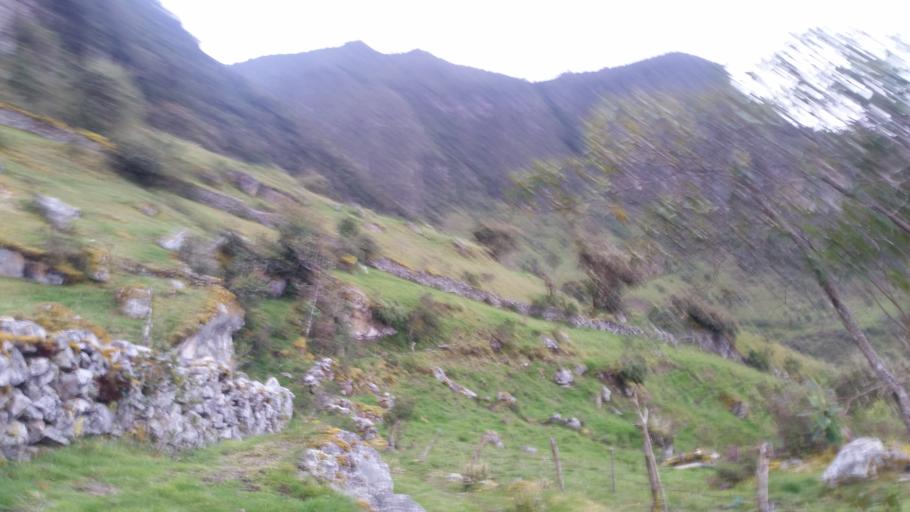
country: CO
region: Cundinamarca
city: Choachi
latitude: 4.5551
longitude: -73.9706
